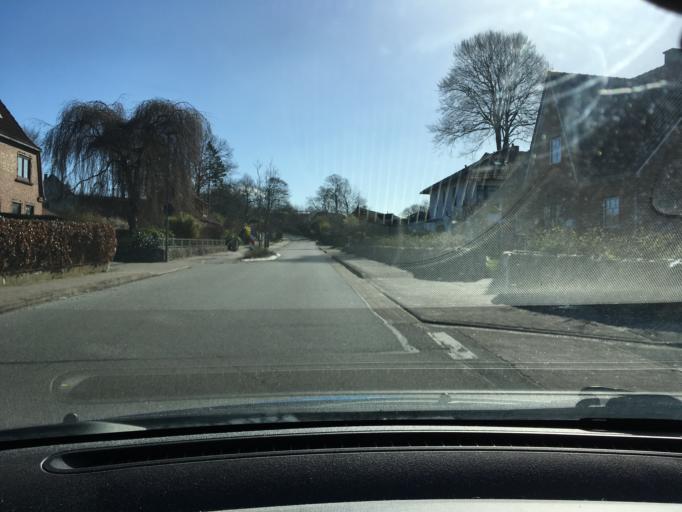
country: DE
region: Schleswig-Holstein
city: Fahrdorf
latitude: 54.5048
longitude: 9.6046
